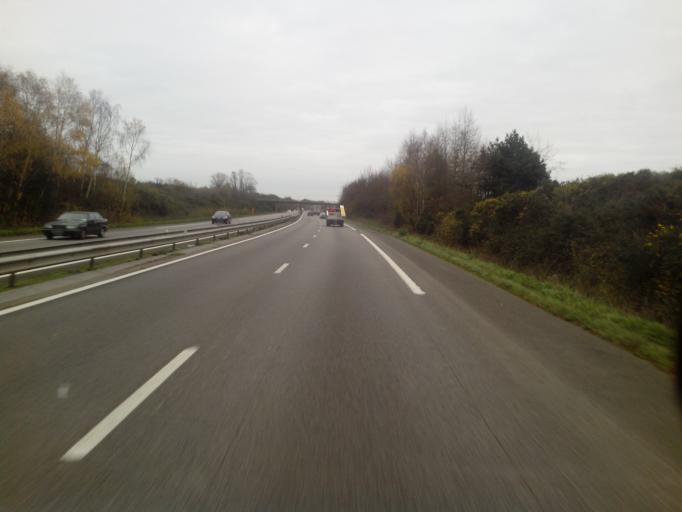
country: FR
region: Pays de la Loire
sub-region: Departement de la Loire-Atlantique
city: Treillieres
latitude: 47.3030
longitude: -1.6319
